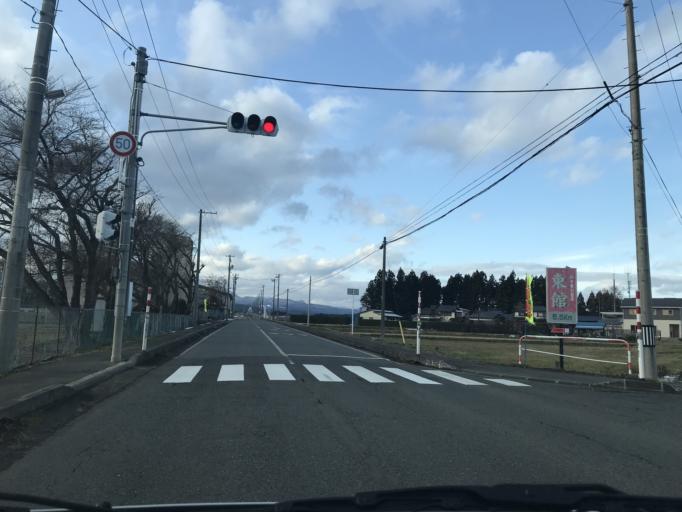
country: JP
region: Iwate
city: Mizusawa
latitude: 39.1969
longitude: 141.0690
